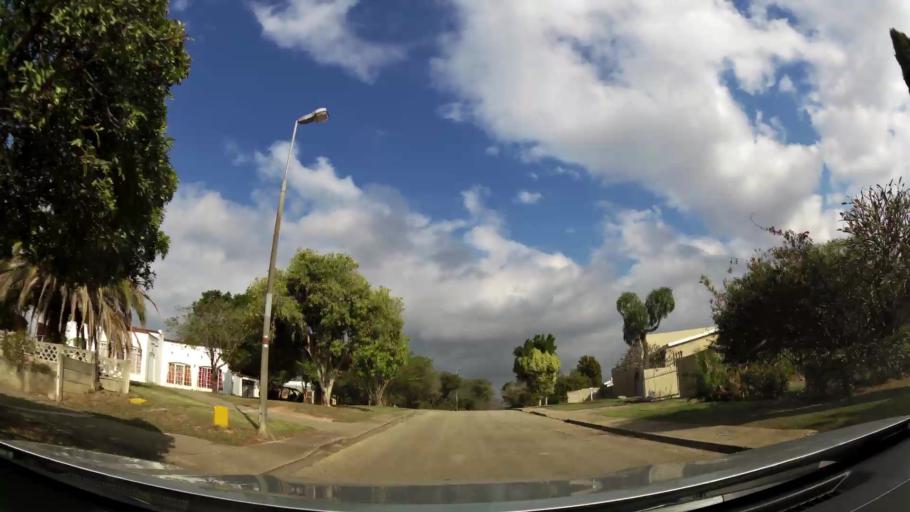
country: ZA
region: Eastern Cape
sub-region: Nelson Mandela Bay Metropolitan Municipality
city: Uitenhage
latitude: -33.7328
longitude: 25.4066
